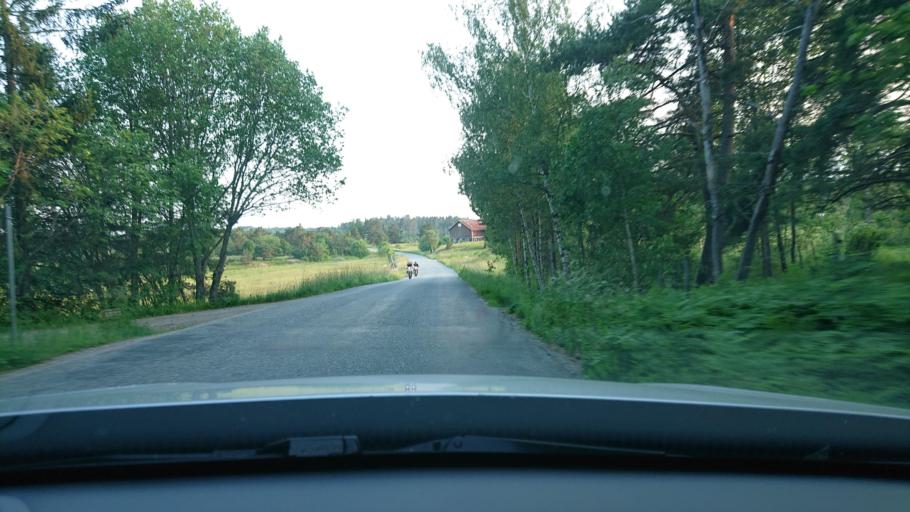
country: SE
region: Stockholm
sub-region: Osterakers Kommun
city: Akersberga
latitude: 59.5110
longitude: 18.3153
